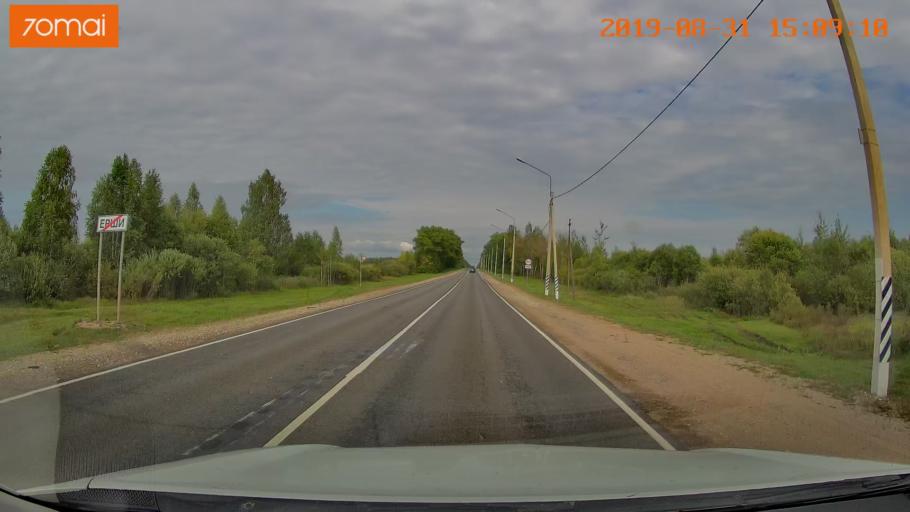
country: RU
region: Kaluga
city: Spas-Demensk
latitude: 54.3989
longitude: 34.1957
